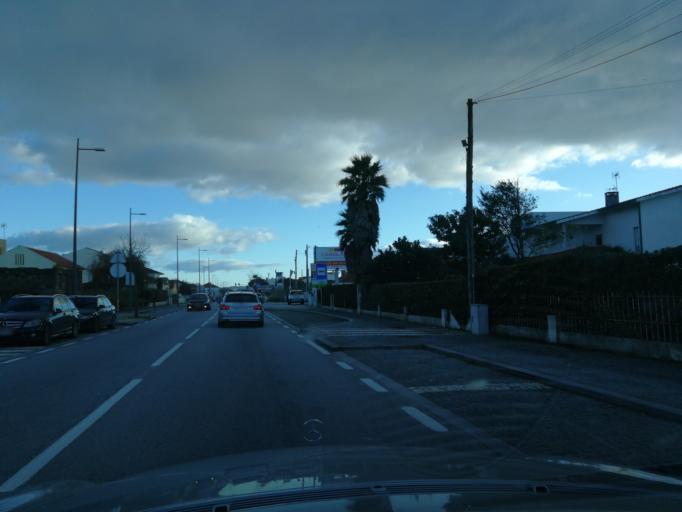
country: PT
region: Viana do Castelo
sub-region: Viana do Castelo
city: Viana do Castelo
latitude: 41.7000
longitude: -8.8465
